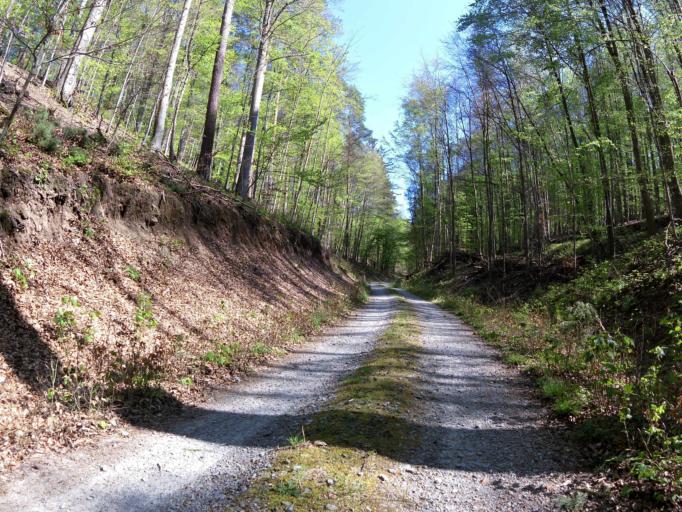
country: DE
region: Thuringia
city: Krauthausen
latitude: 50.9841
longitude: 10.2538
